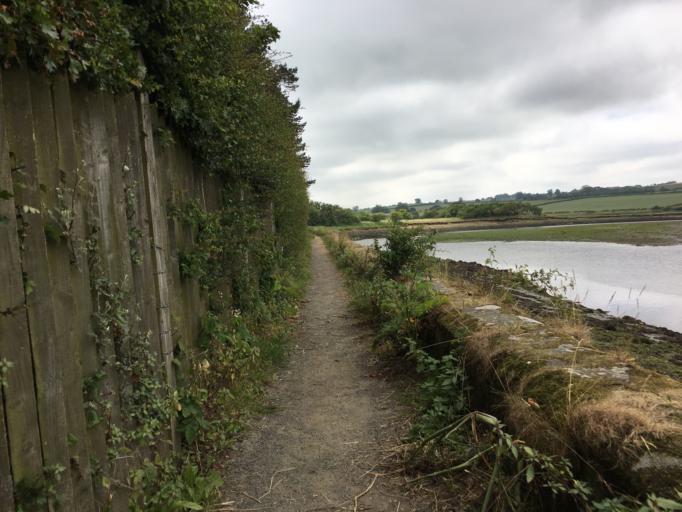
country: GB
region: England
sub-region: Northumberland
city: Alnmouth
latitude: 55.3904
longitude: -1.6171
